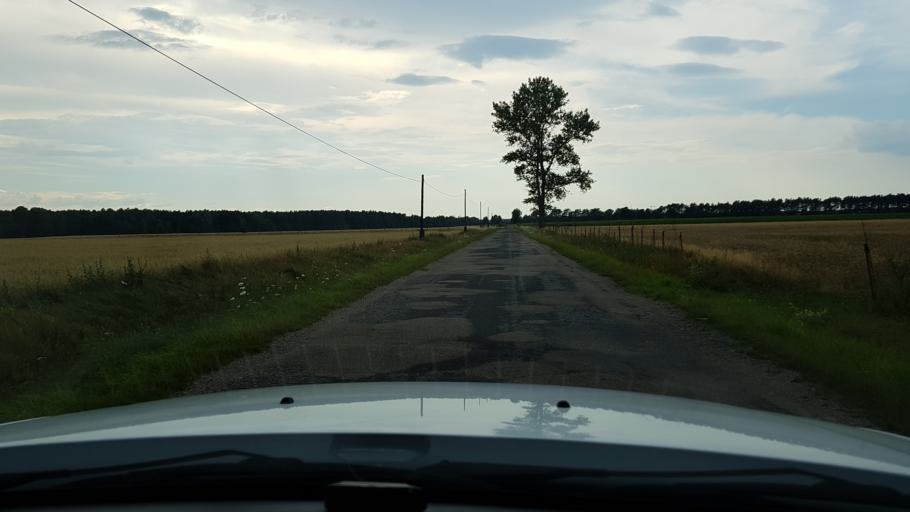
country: PL
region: West Pomeranian Voivodeship
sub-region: Powiat drawski
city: Czaplinek
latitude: 53.4317
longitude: 16.3007
